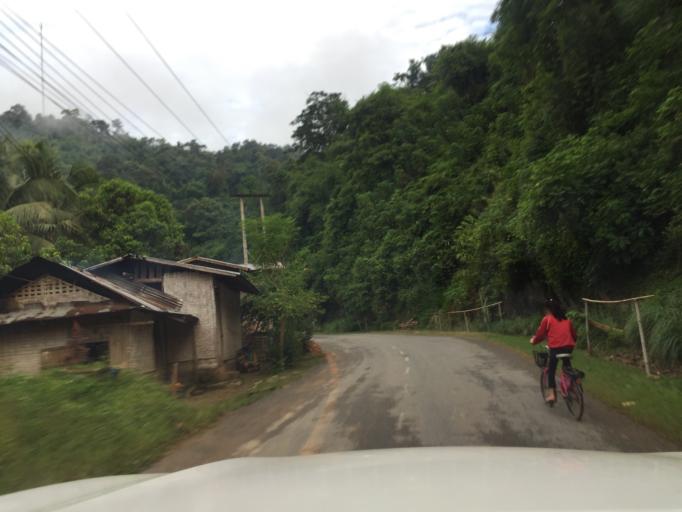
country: LA
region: Phongsali
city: Khoa
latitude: 21.1029
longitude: 102.2583
